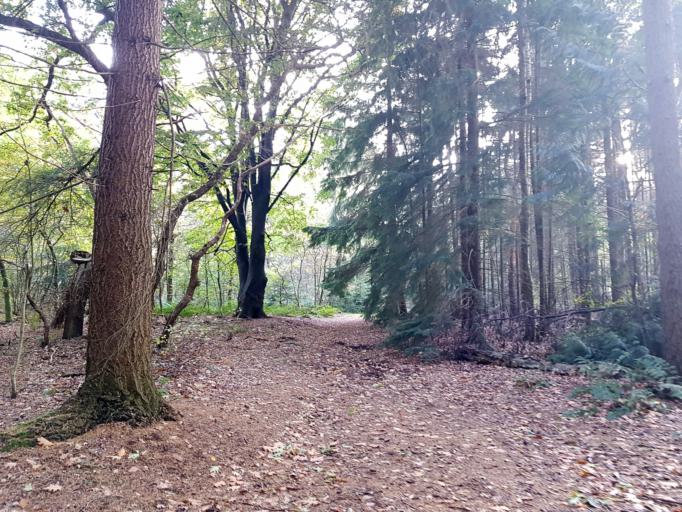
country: NL
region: Utrecht
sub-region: Gemeente Utrechtse Heuvelrug
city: Leersum
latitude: 52.0274
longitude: 5.4046
